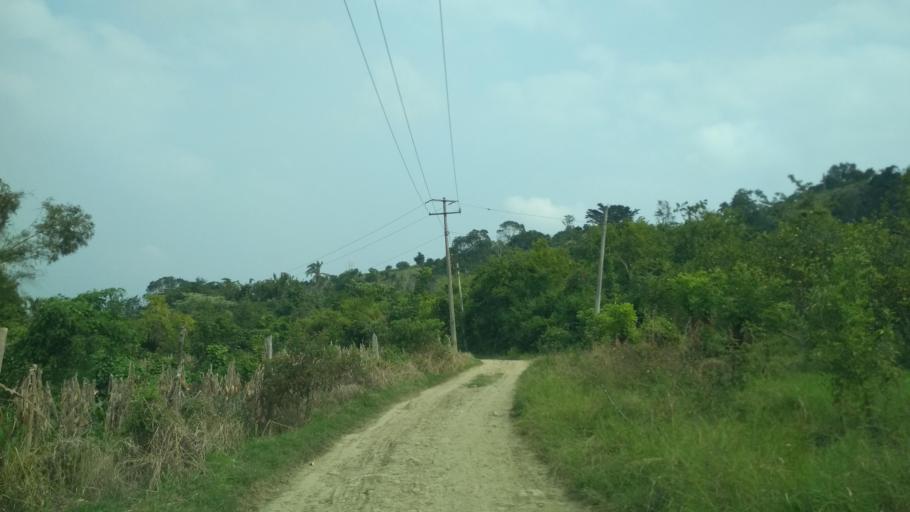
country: MM
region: Kayah
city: Loikaw
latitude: 20.2081
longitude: 97.3158
